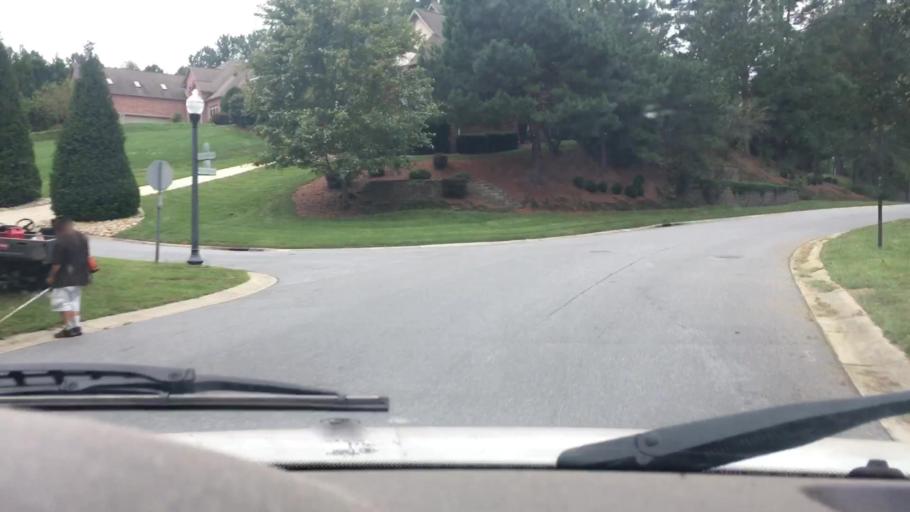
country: US
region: North Carolina
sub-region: Lincoln County
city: Denver
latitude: 35.4816
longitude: -81.0277
